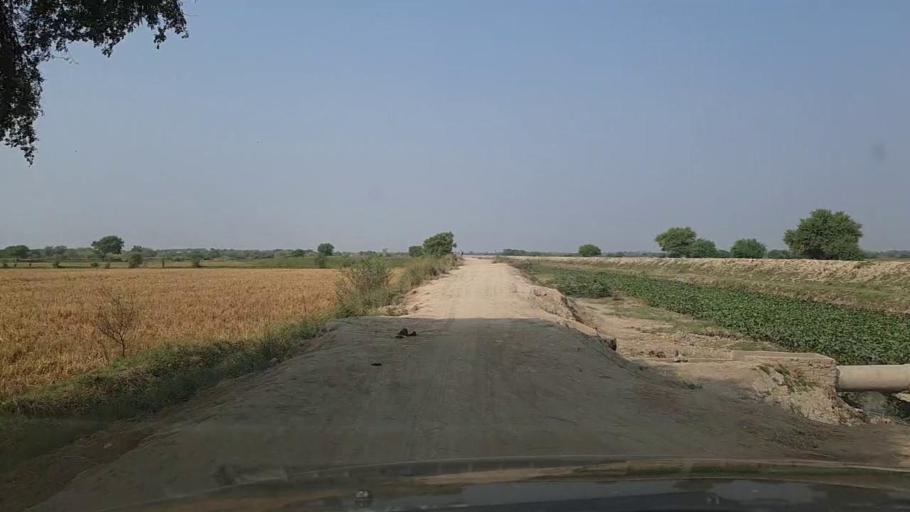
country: PK
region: Sindh
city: Mirpur Batoro
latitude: 24.6810
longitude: 68.2485
